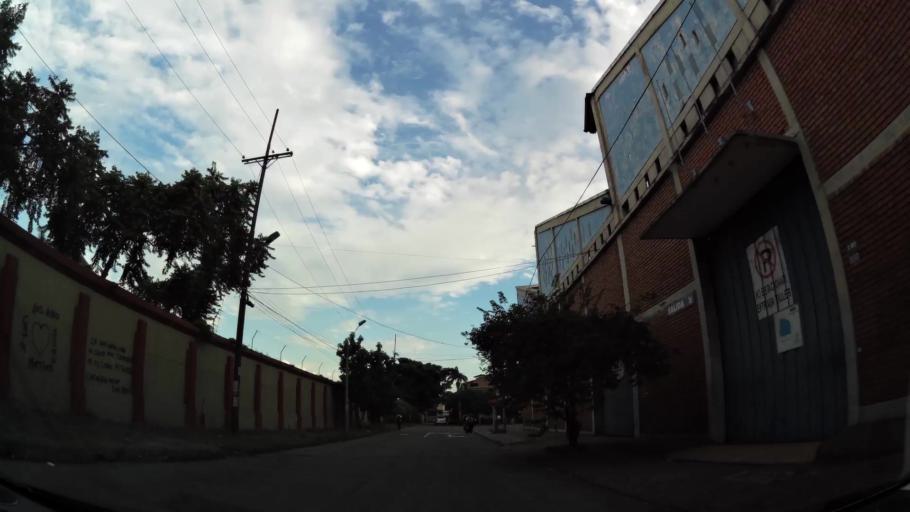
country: CO
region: Valle del Cauca
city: Cali
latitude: 3.4607
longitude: -76.5191
